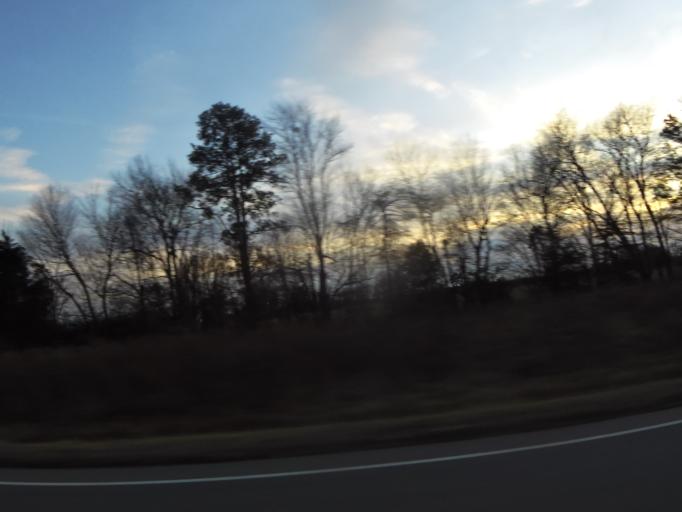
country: US
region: Virginia
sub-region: Southampton County
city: Courtland
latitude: 36.7832
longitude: -77.1183
